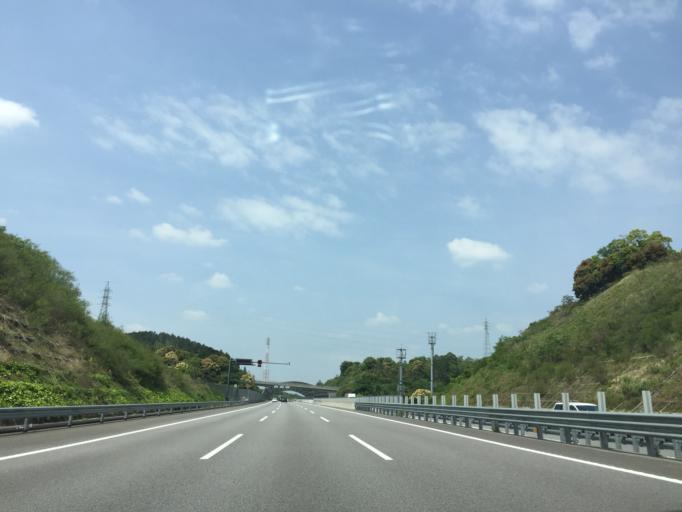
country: JP
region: Shizuoka
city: Hamakita
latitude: 34.8389
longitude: 137.7839
